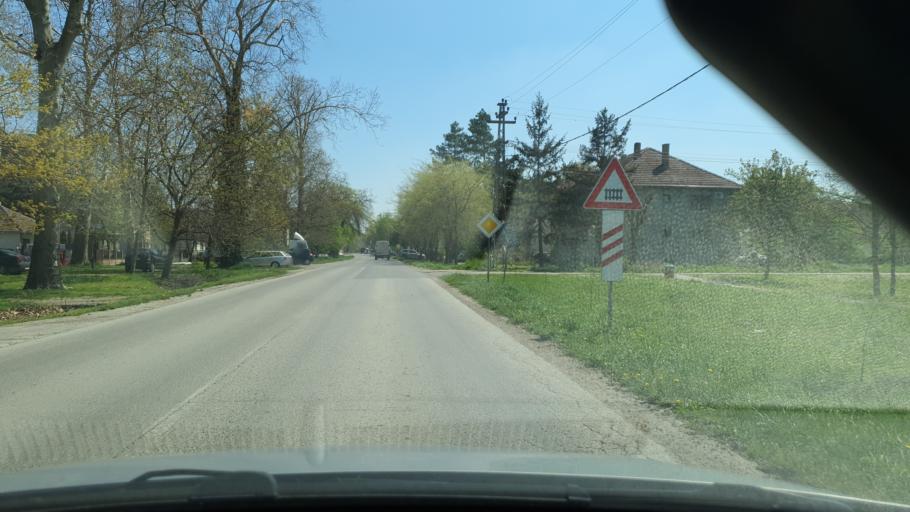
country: RS
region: Autonomna Pokrajina Vojvodina
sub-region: Zapadnobacki Okrug
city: Odzaci
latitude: 45.5118
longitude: 19.2519
